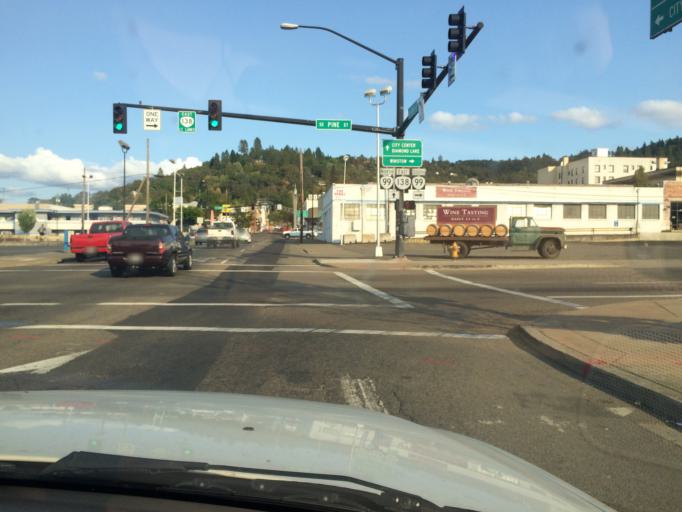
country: US
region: Oregon
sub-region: Douglas County
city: Roseburg
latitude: 43.2100
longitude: -123.3472
